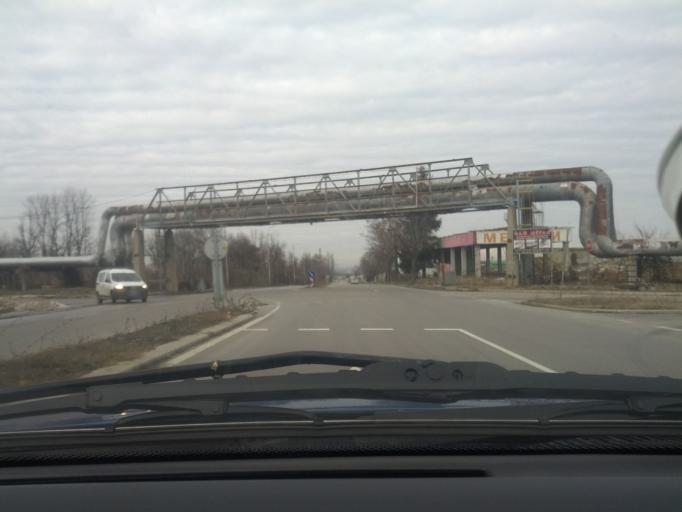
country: BG
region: Vratsa
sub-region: Obshtina Vratsa
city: Vratsa
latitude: 43.1971
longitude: 23.5734
